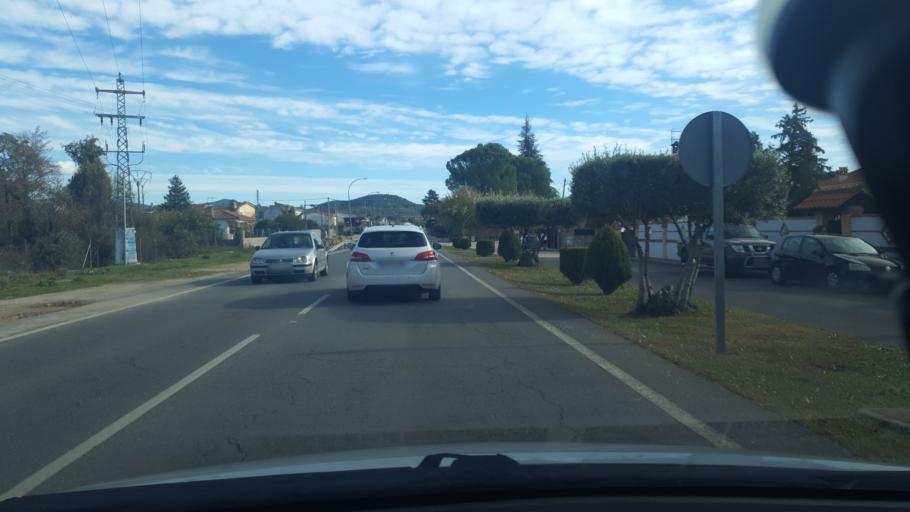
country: ES
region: Castille and Leon
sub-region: Provincia de Avila
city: La Adrada
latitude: 40.3053
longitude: -4.6452
